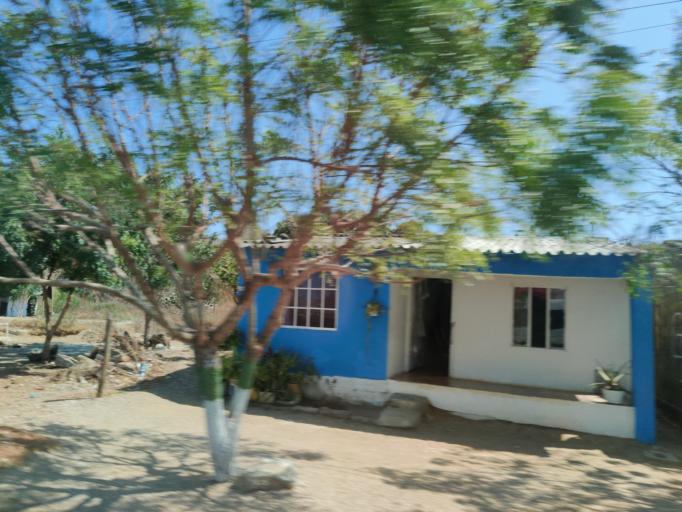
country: CO
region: Bolivar
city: Santa Catalina
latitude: 10.7449
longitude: -75.2636
